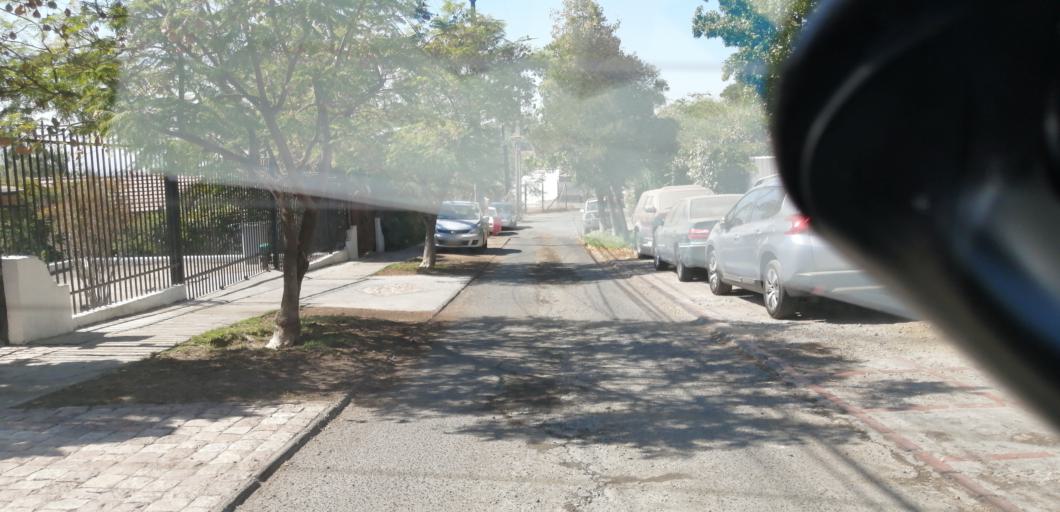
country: CL
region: Santiago Metropolitan
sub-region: Provincia de Santiago
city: Lo Prado
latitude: -33.4547
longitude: -70.8231
